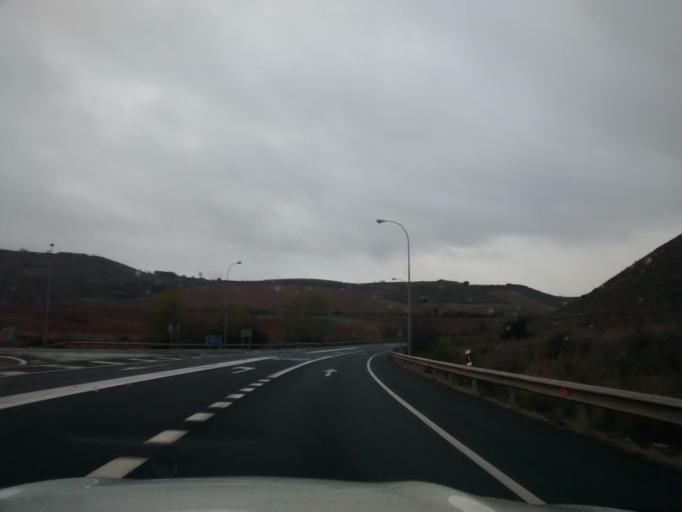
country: ES
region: La Rioja
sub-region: Provincia de La Rioja
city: Cenicero
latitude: 42.4713
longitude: -2.6396
